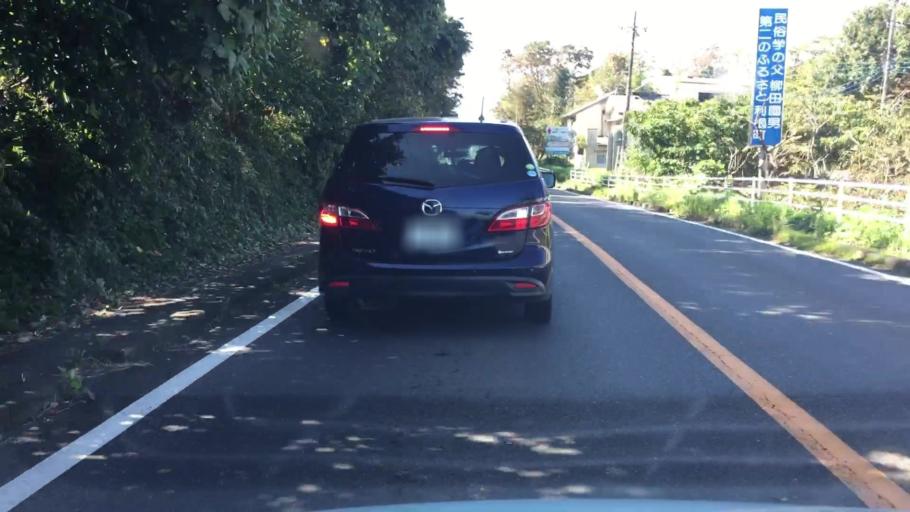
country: JP
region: Ibaraki
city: Ryugasaki
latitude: 35.8575
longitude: 140.1422
